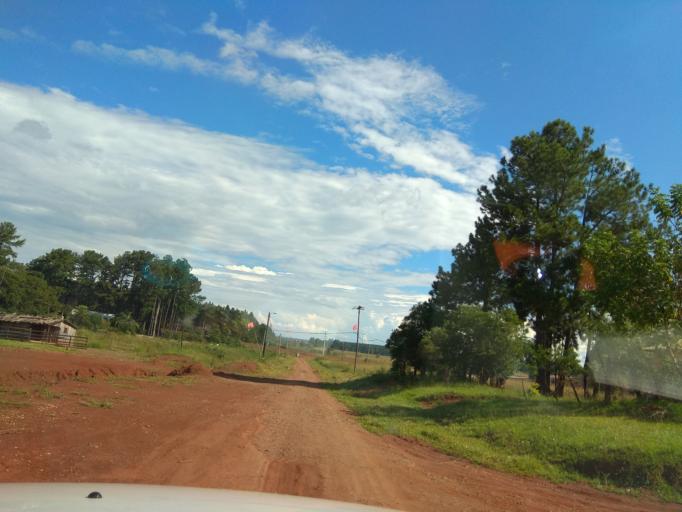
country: AR
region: Misiones
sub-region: Departamento de Candelaria
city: Candelaria
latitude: -27.4679
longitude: -55.7562
